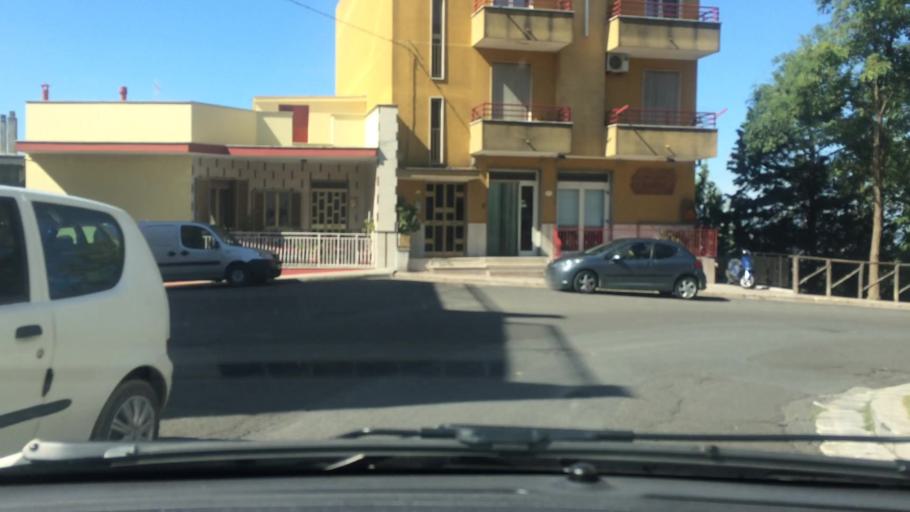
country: IT
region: Basilicate
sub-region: Provincia di Matera
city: Montescaglioso
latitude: 40.5495
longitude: 16.6658
